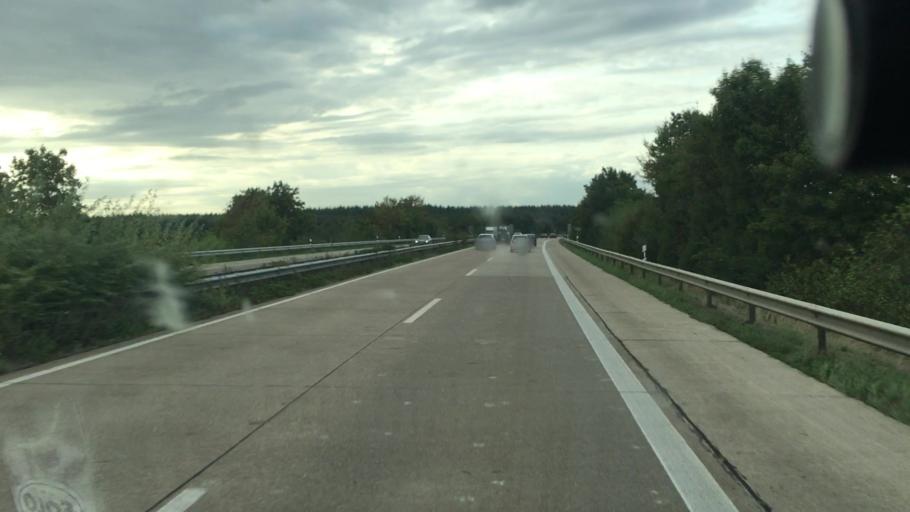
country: DE
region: Lower Saxony
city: Emstek
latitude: 52.8869
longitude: 8.1821
